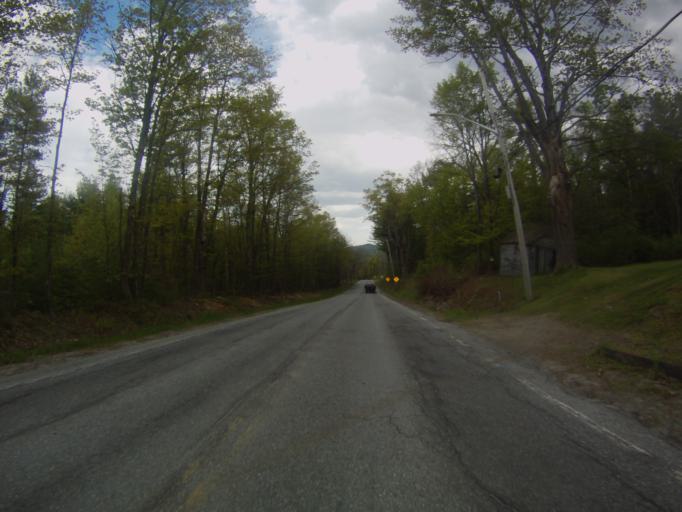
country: US
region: New York
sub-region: Essex County
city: Mineville
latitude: 44.0793
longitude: -73.5281
